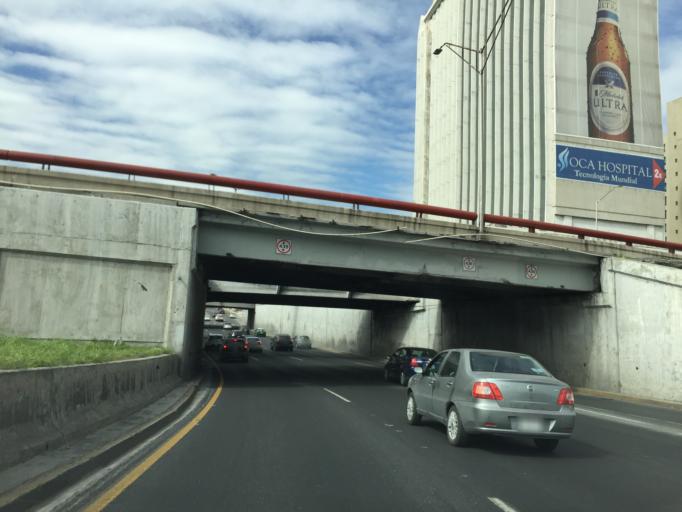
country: MX
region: Nuevo Leon
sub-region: Monterrey
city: Monterrey
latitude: 25.6654
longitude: -100.3193
